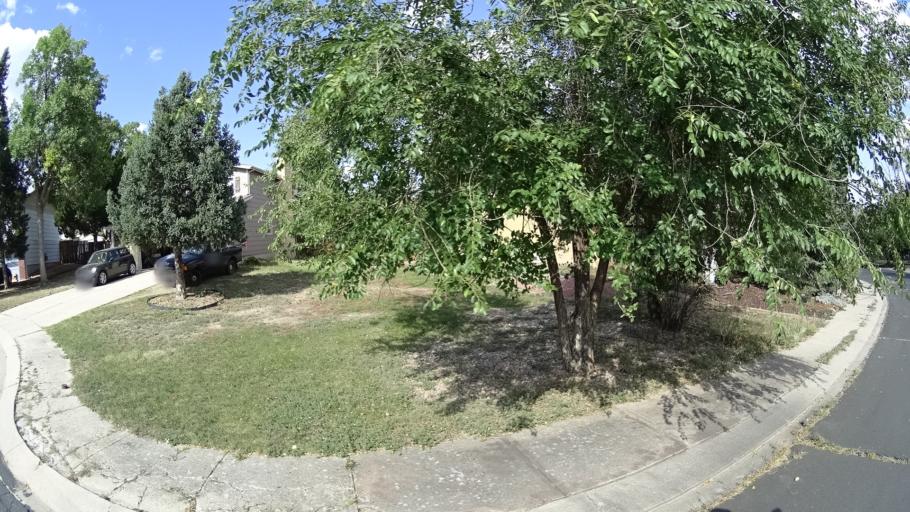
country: US
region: Colorado
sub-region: El Paso County
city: Cimarron Hills
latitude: 38.8705
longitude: -104.7255
